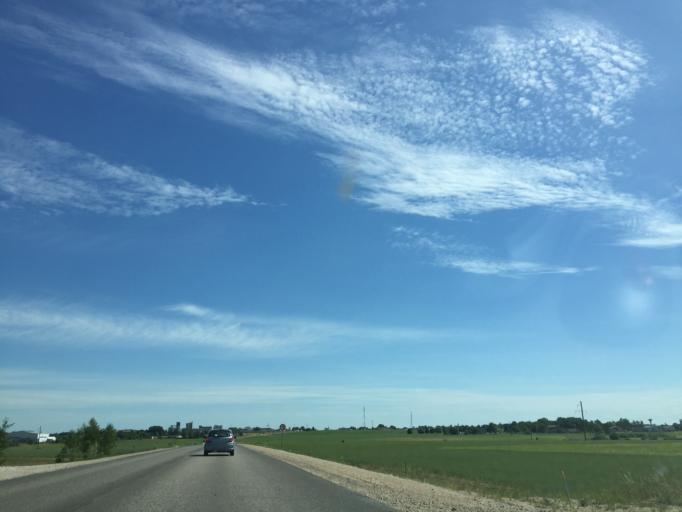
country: LV
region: Saldus Rajons
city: Saldus
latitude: 56.6748
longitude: 22.4400
